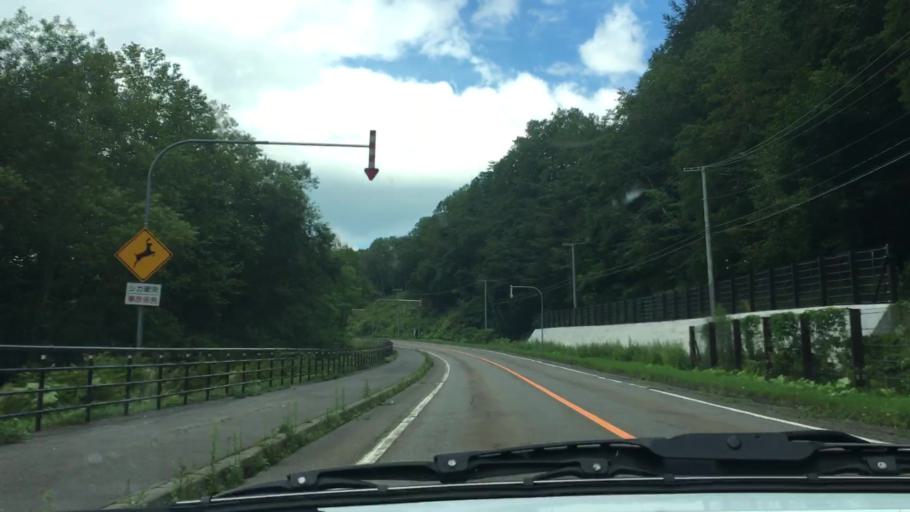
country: JP
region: Hokkaido
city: Otofuke
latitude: 43.3617
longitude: 143.2471
